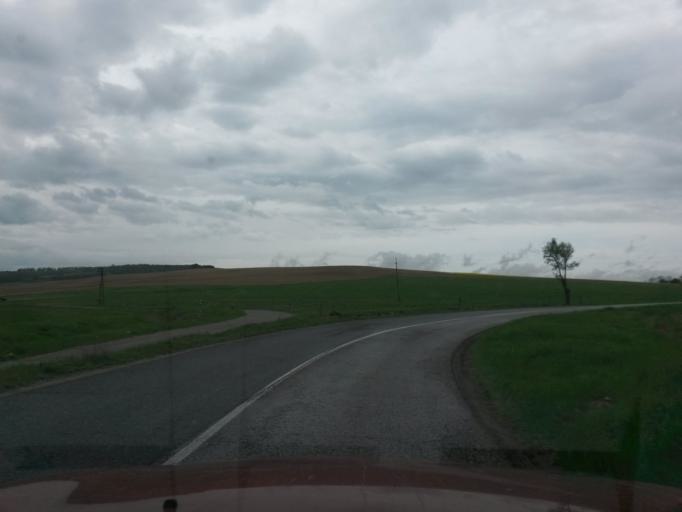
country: SK
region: Kosicky
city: Moldava nad Bodvou
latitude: 48.5314
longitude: 21.1057
